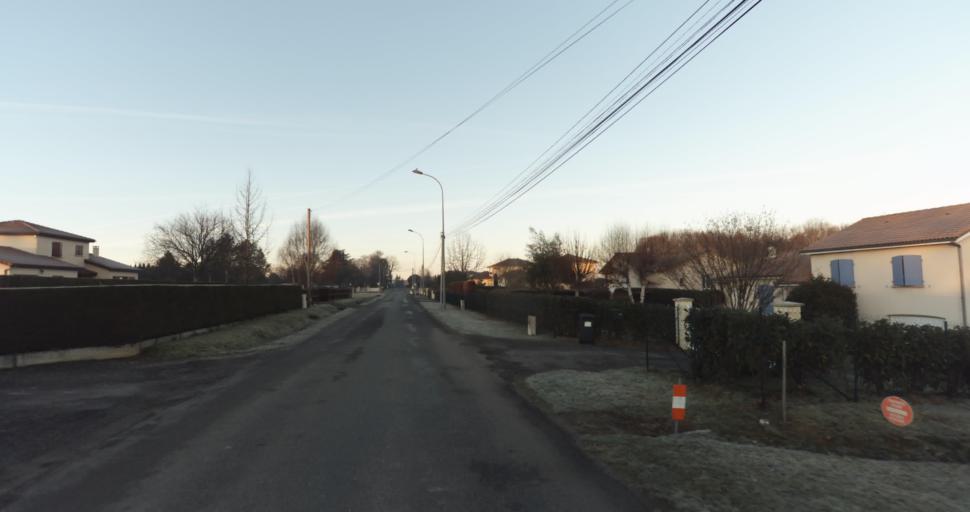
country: FR
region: Limousin
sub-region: Departement de la Haute-Vienne
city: Aixe-sur-Vienne
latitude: 45.8144
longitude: 1.1381
